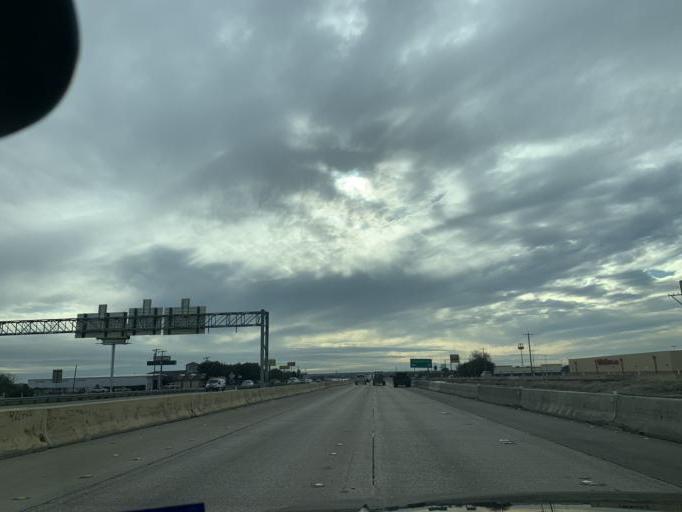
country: US
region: Texas
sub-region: Dallas County
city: Duncanville
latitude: 32.6459
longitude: -96.8866
